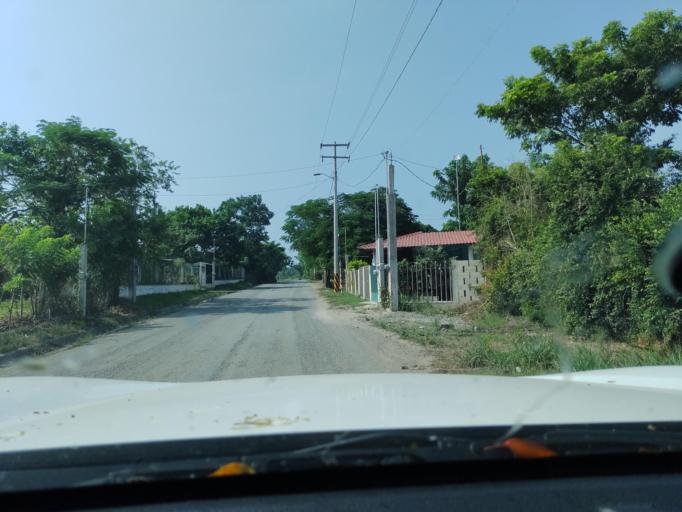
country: MX
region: Veracruz
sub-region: Martinez de la Torre
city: El Progreso
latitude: 20.0767
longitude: -97.0062
